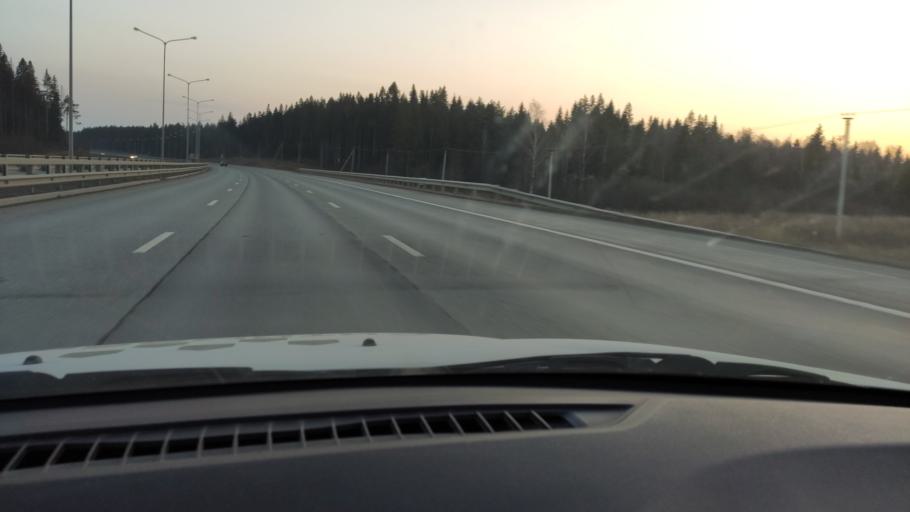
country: RU
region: Perm
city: Lobanovo
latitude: 57.8628
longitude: 56.2590
